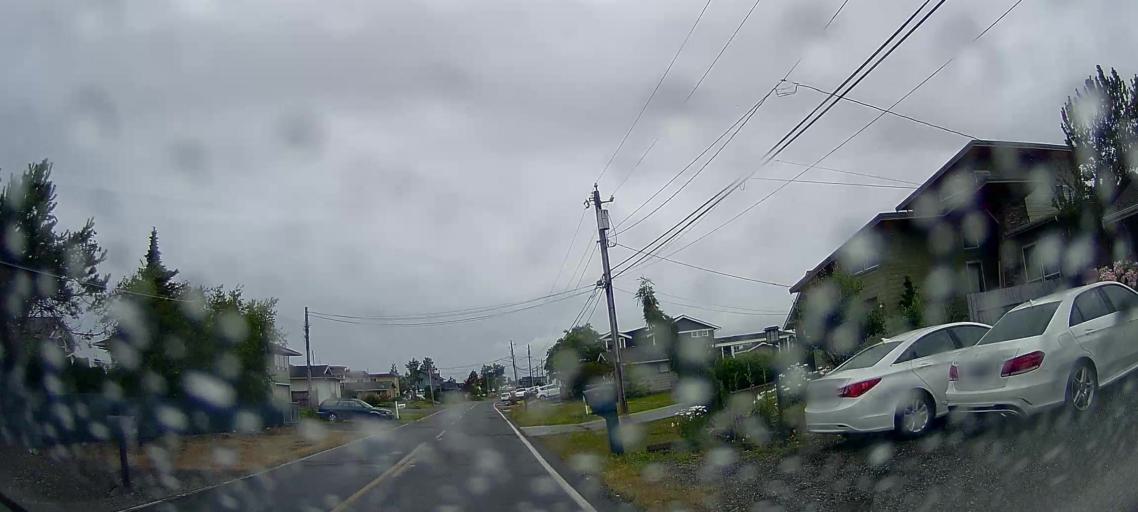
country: US
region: Washington
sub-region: Whatcom County
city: Marietta
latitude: 48.7927
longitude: -122.7045
